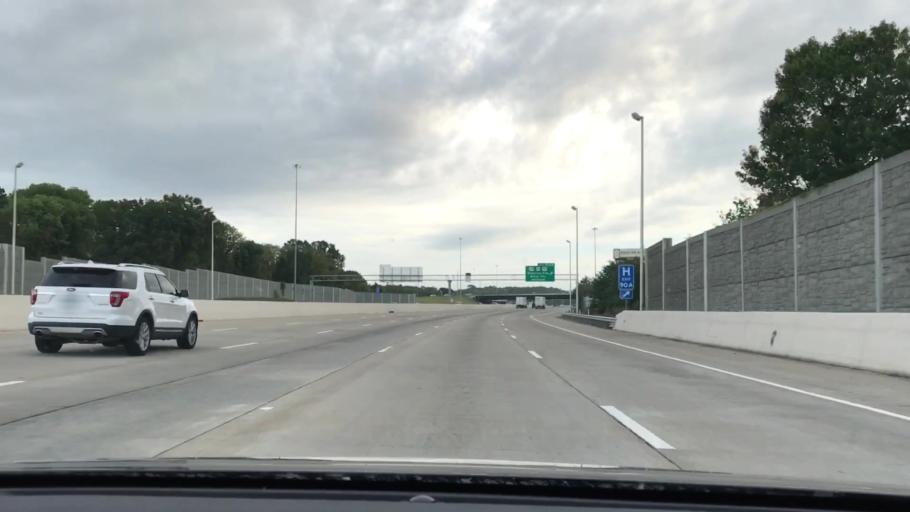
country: US
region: Tennessee
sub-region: Davidson County
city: Nashville
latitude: 36.2355
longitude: -86.7640
